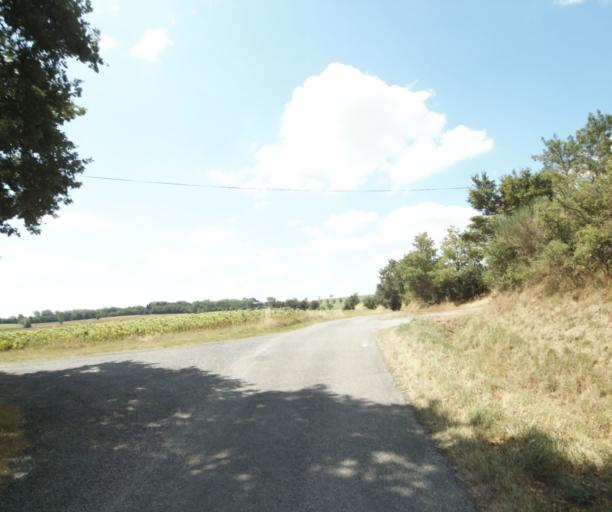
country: FR
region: Midi-Pyrenees
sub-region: Departement de la Haute-Garonne
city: Auriac-sur-Vendinelle
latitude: 43.4749
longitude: 1.7963
